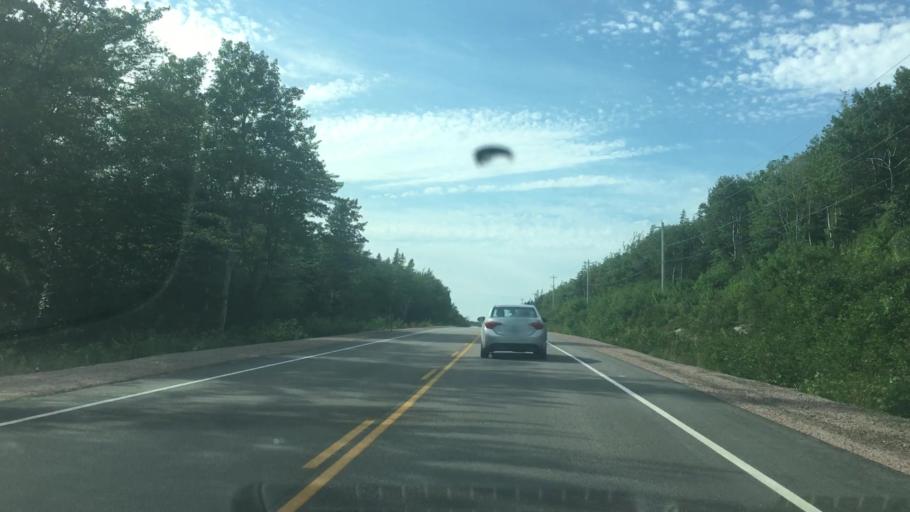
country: CA
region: Nova Scotia
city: Sydney Mines
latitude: 46.8180
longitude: -60.3476
